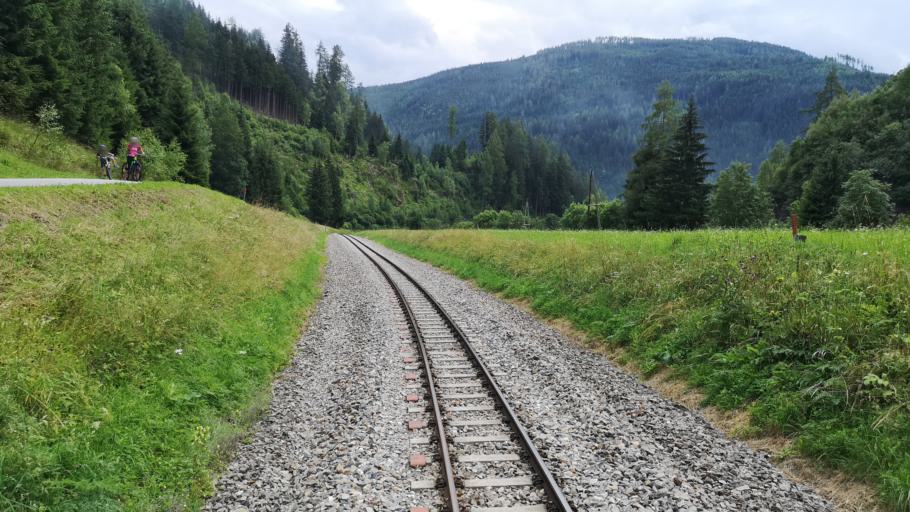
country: AT
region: Salzburg
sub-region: Politischer Bezirk Tamsweg
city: Ramingstein
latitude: 47.0828
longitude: 13.8135
